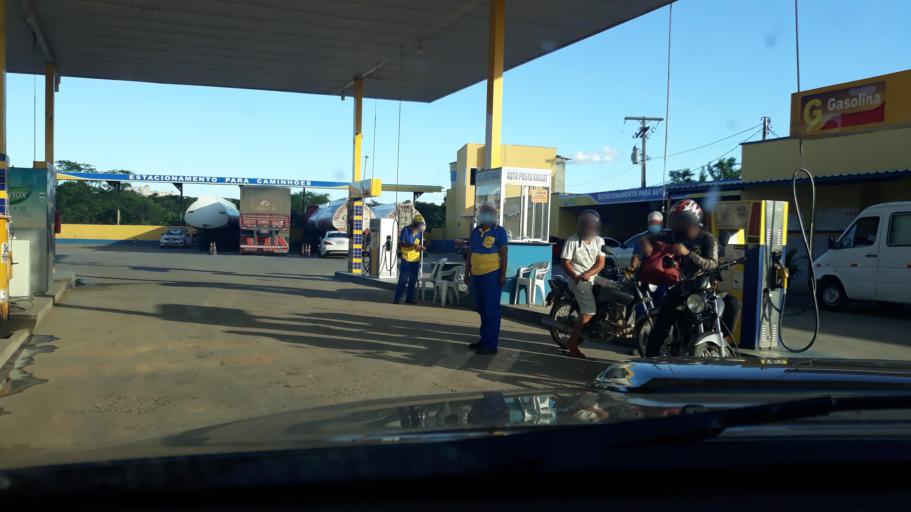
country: BR
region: Bahia
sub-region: Riacho De Santana
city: Riacho de Santana
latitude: -13.7648
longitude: -42.7279
